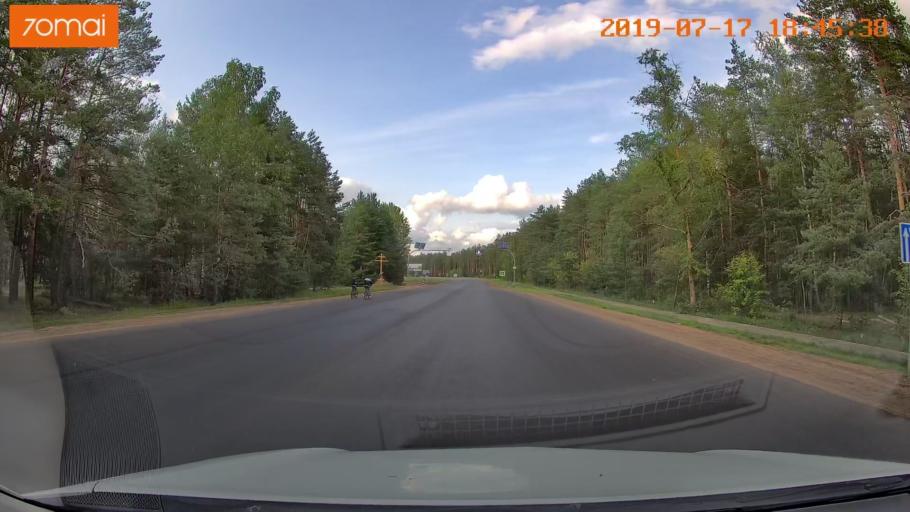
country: BY
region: Mogilev
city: Asipovichy
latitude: 53.3264
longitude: 28.6570
